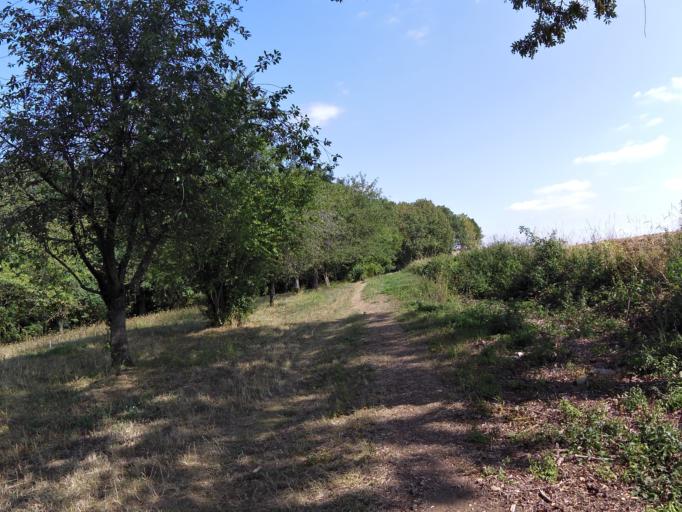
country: DE
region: Bavaria
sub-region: Regierungsbezirk Unterfranken
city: Theilheim
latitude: 49.7572
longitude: 10.0179
